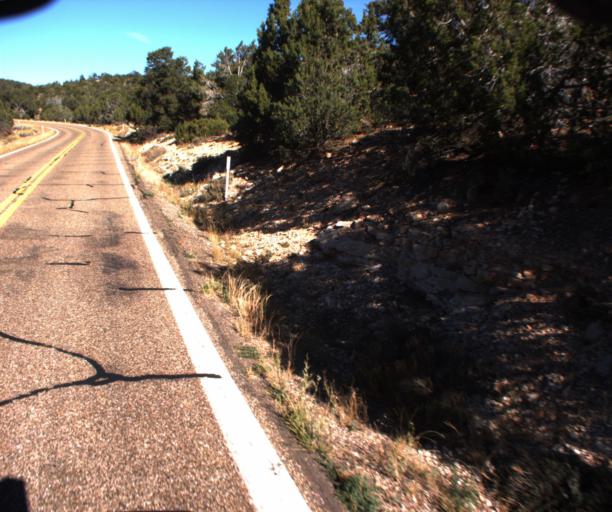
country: US
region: Arizona
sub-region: Coconino County
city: Fredonia
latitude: 36.7403
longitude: -112.1075
